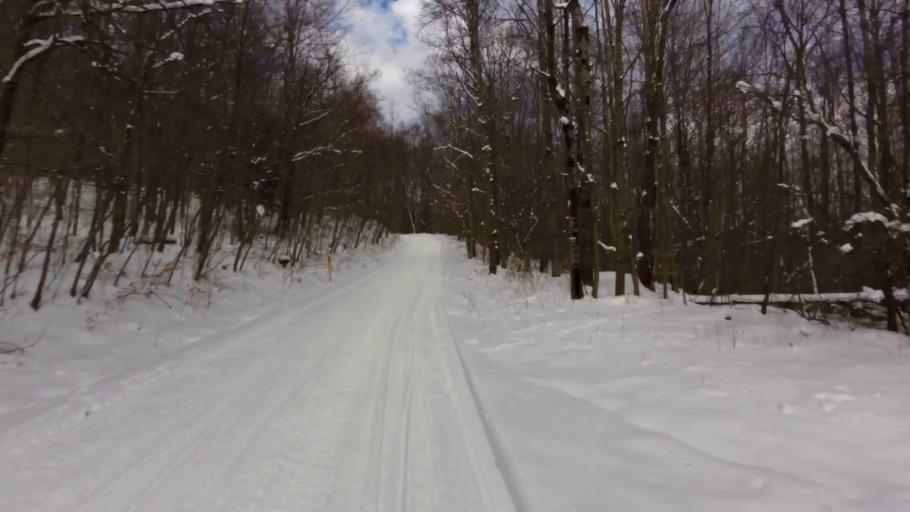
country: US
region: Pennsylvania
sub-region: McKean County
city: Bradford
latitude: 42.0325
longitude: -78.7031
